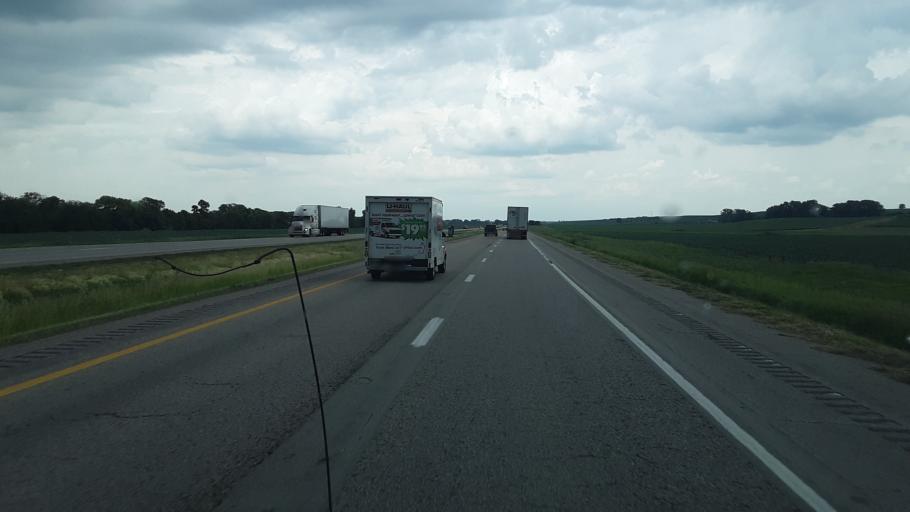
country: US
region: Iowa
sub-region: Pottawattamie County
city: Council Bluffs
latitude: 41.4157
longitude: -95.6456
